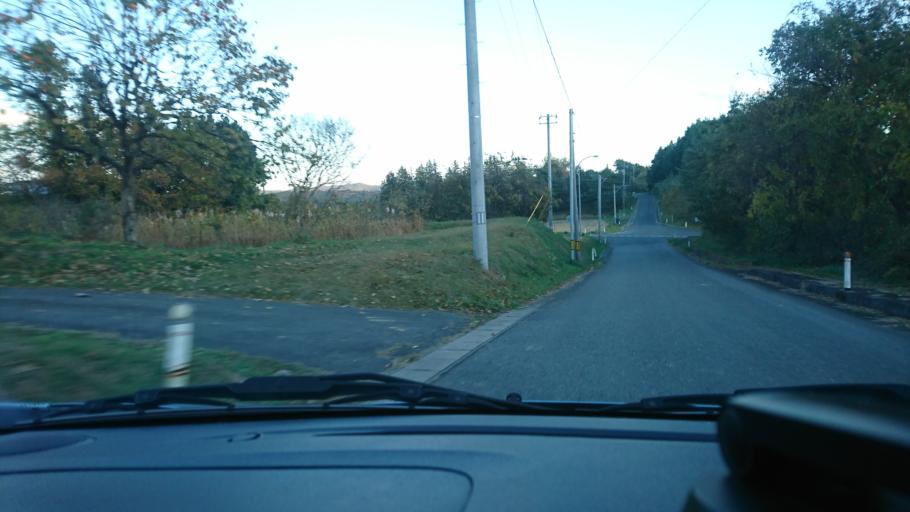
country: JP
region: Iwate
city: Ichinoseki
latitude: 38.7674
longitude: 141.2371
